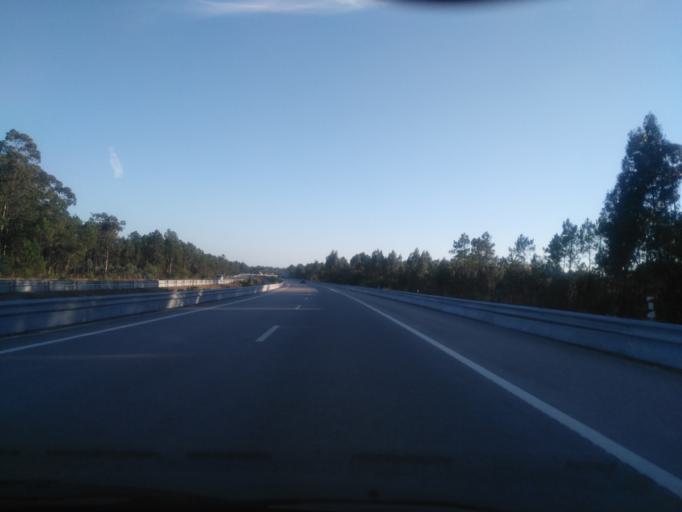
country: PT
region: Coimbra
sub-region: Figueira da Foz
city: Alhadas
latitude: 40.2444
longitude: -8.7830
